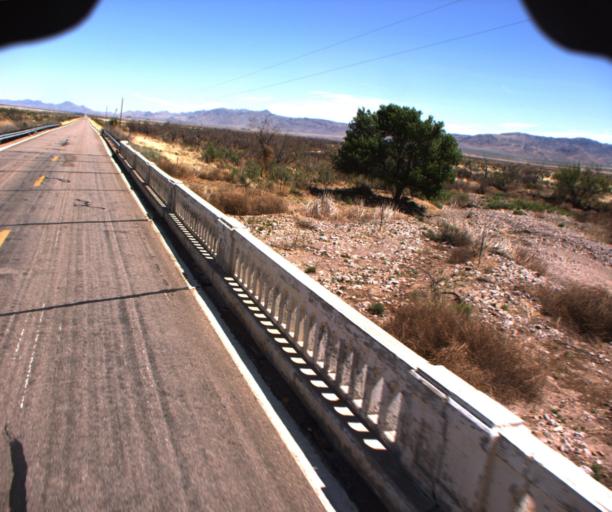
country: US
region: Arizona
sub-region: Cochise County
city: Douglas
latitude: 31.6992
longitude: -109.1268
